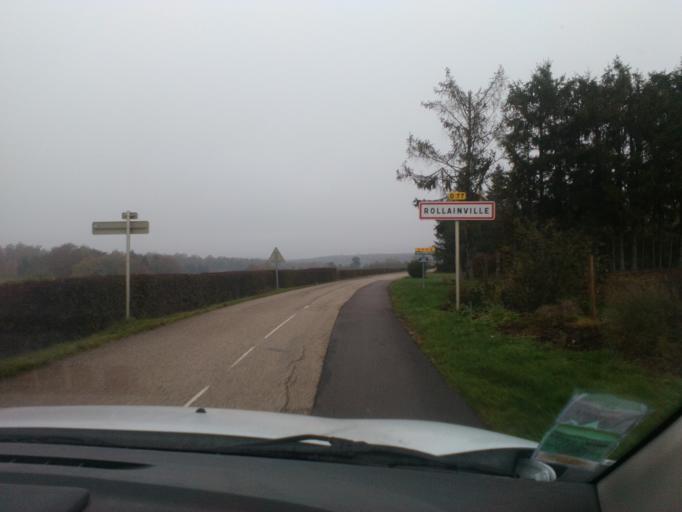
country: FR
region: Lorraine
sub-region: Departement des Vosges
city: Neufchateau
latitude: 48.3545
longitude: 5.7317
